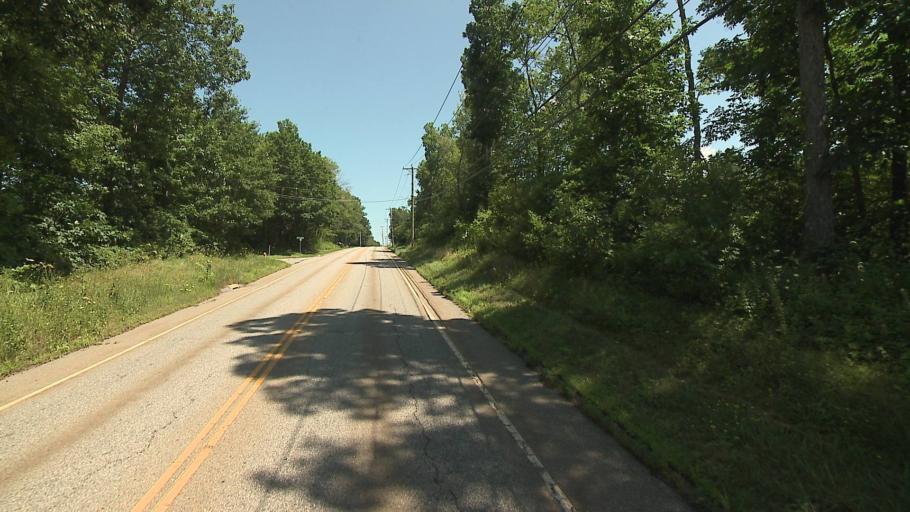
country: US
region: Connecticut
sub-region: Litchfield County
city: Northwest Harwinton
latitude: 41.7768
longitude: -73.0179
